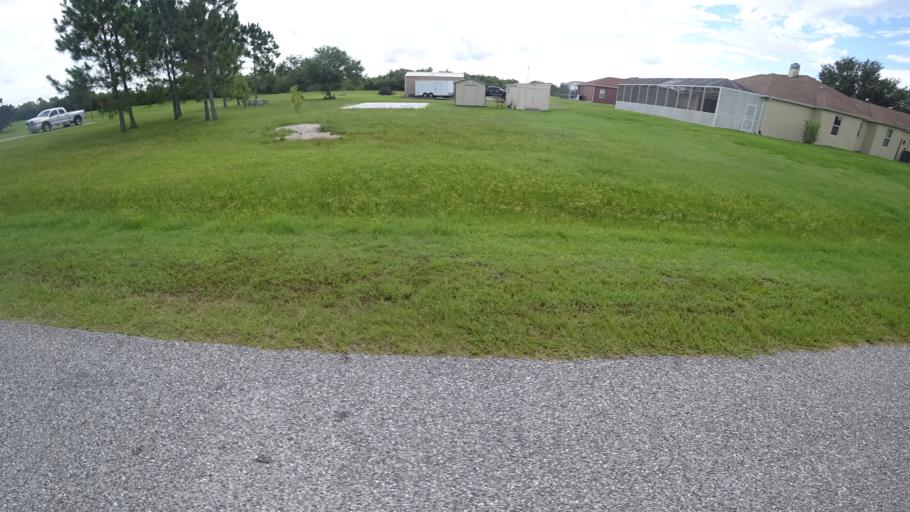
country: US
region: Florida
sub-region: Sarasota County
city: Lake Sarasota
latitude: 27.3898
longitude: -82.2763
